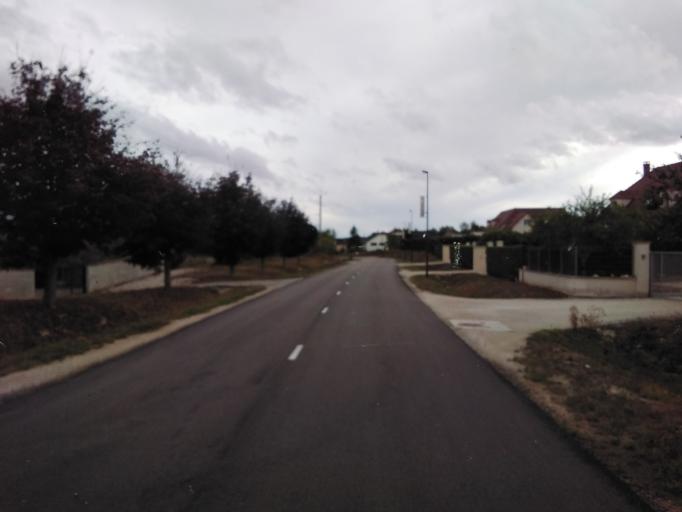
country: FR
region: Champagne-Ardenne
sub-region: Departement de l'Aube
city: Les Riceys
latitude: 47.9831
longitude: 4.3592
